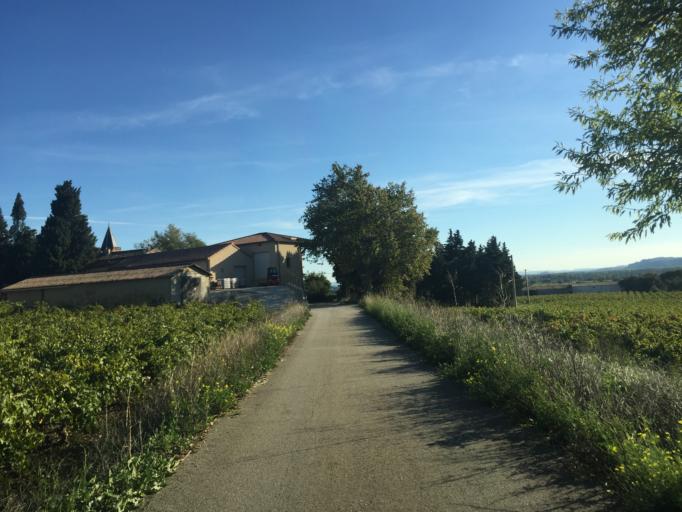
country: FR
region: Provence-Alpes-Cote d'Azur
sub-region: Departement du Vaucluse
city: Chateauneuf-du-Pape
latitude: 44.0524
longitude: 4.8381
